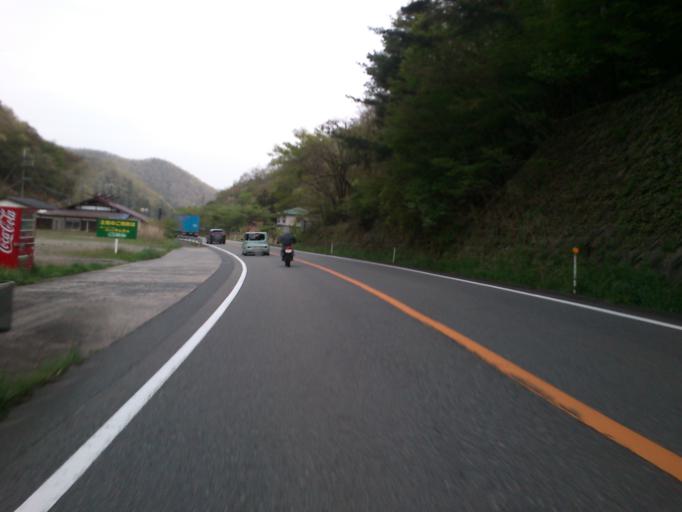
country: JP
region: Hyogo
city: Sasayama
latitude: 35.1335
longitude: 135.3320
